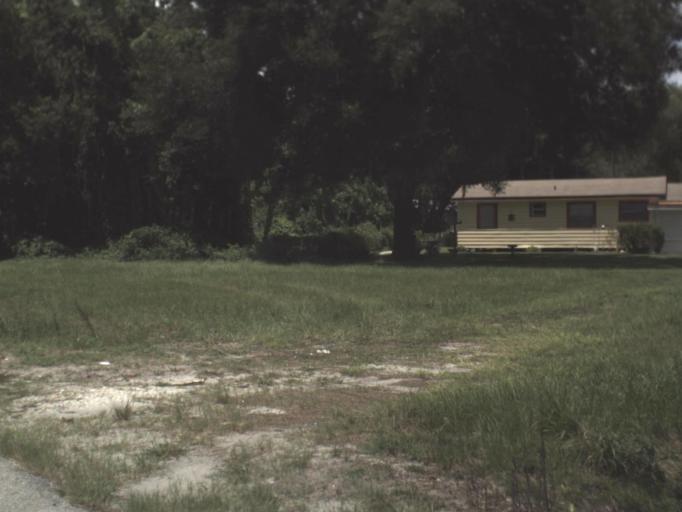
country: US
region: Florida
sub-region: Hillsborough County
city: Plant City
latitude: 28.0286
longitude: -82.1555
